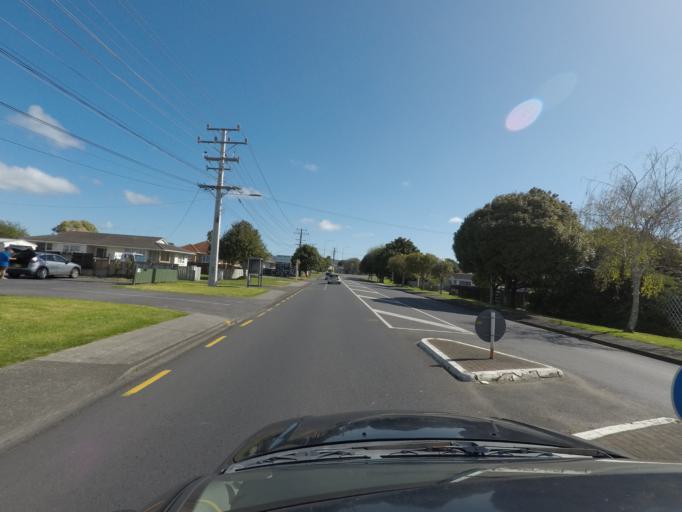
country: NZ
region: Auckland
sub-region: Auckland
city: Rosebank
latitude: -36.8627
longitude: 174.6069
